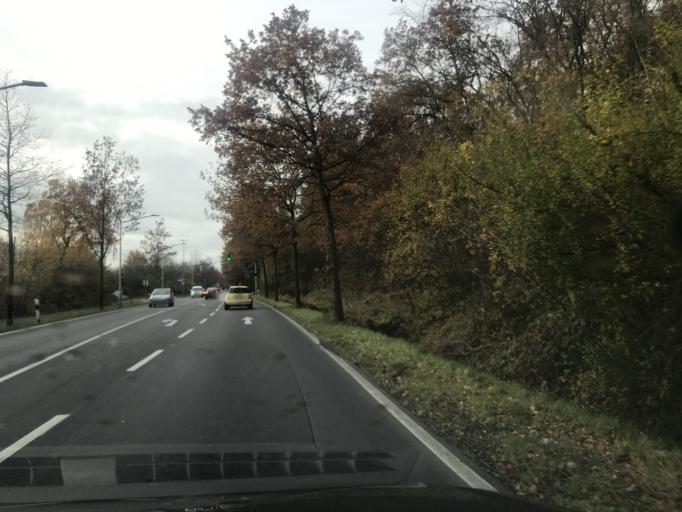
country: DE
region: North Rhine-Westphalia
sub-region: Regierungsbezirk Arnsberg
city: Hamm
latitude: 51.6608
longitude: 7.8522
